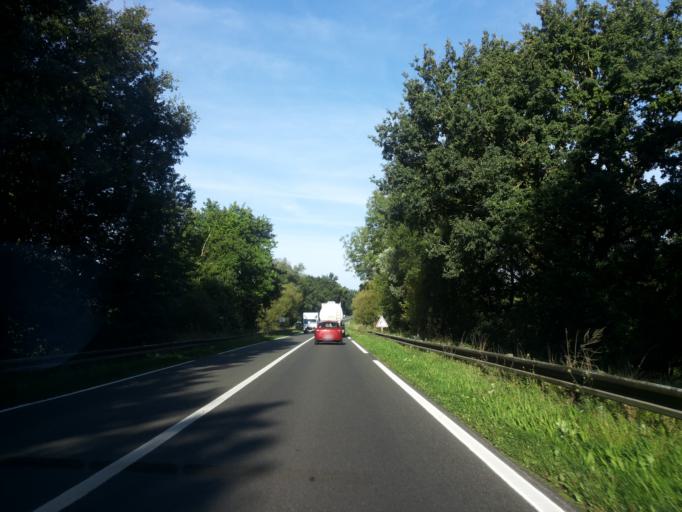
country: FR
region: Picardie
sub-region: Departement de l'Aisne
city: La Fere
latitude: 49.6708
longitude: 3.3555
